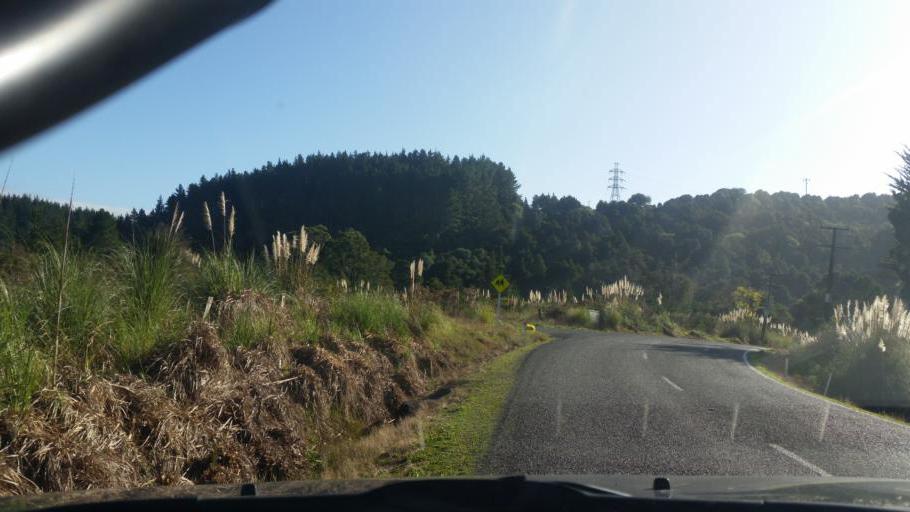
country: NZ
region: Auckland
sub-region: Auckland
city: Wellsford
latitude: -36.2150
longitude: 174.4680
